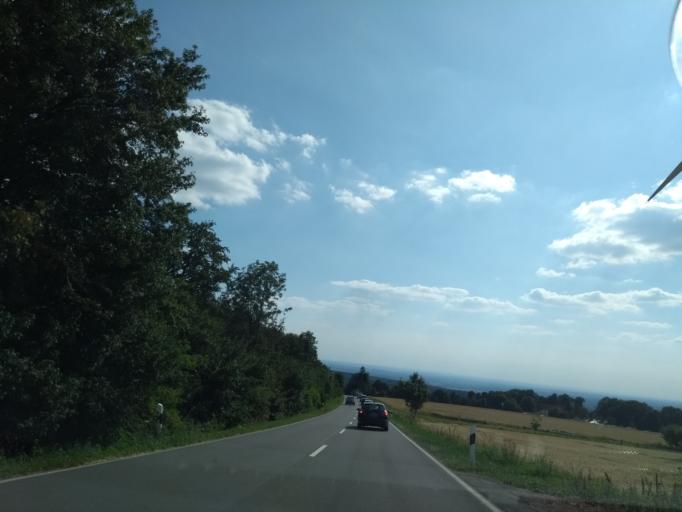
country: DE
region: North Rhine-Westphalia
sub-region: Regierungsbezirk Detmold
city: Altenbeken
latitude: 51.8171
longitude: 8.9108
